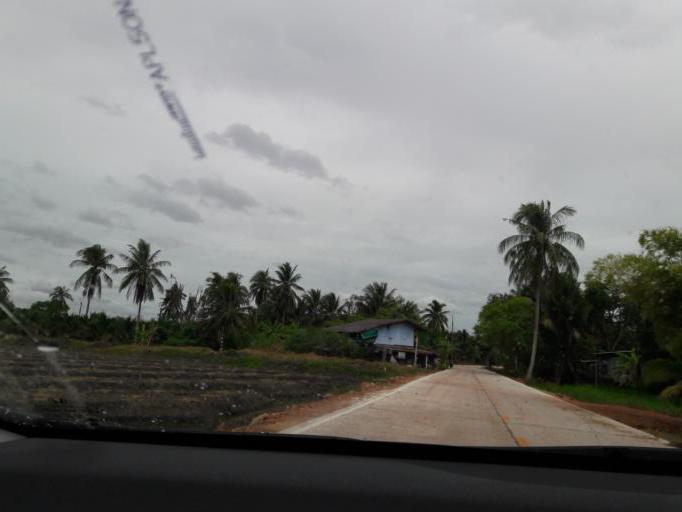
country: TH
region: Samut Sakhon
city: Ban Phaeo
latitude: 13.5424
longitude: 100.0380
